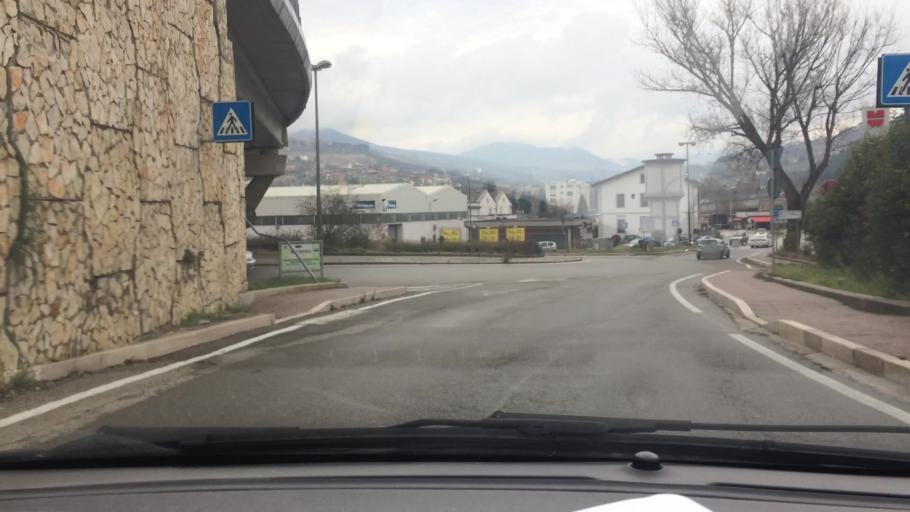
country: IT
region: Basilicate
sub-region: Provincia di Potenza
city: Potenza
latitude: 40.6295
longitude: 15.7966
